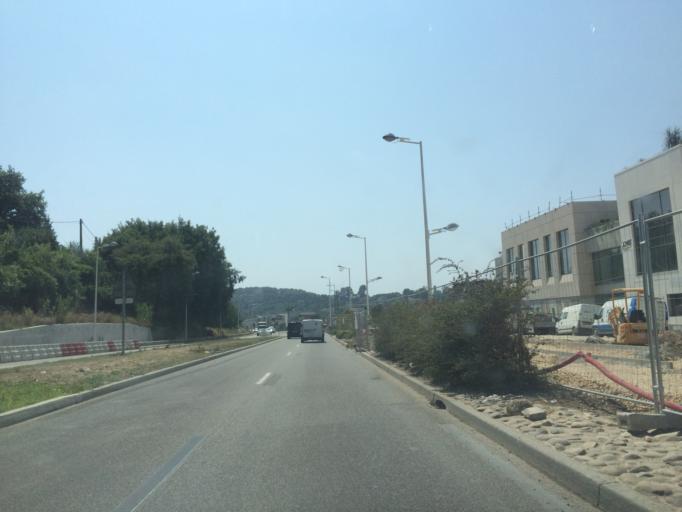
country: FR
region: Provence-Alpes-Cote d'Azur
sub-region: Departement des Alpes-Maritimes
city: Villeneuve-Loubet
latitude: 43.6672
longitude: 7.1272
